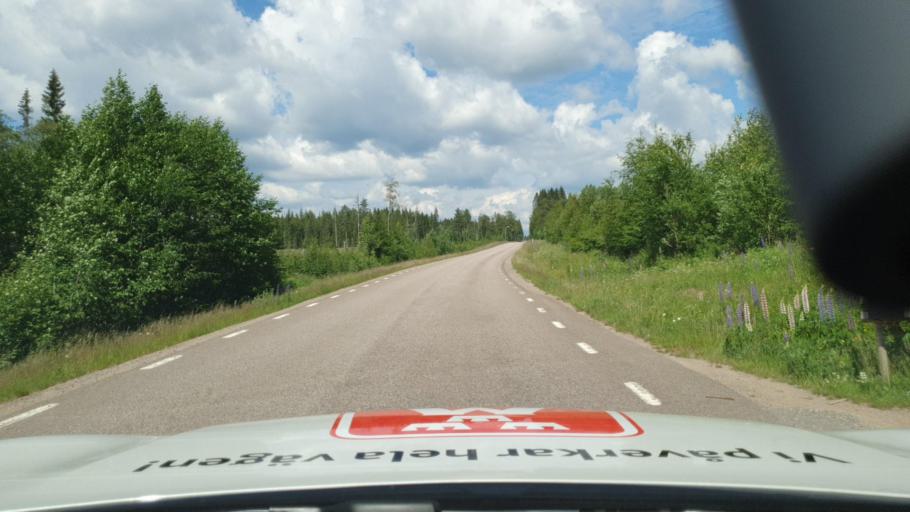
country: SE
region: Vaermland
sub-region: Torsby Kommun
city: Torsby
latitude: 60.4593
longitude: 12.8847
